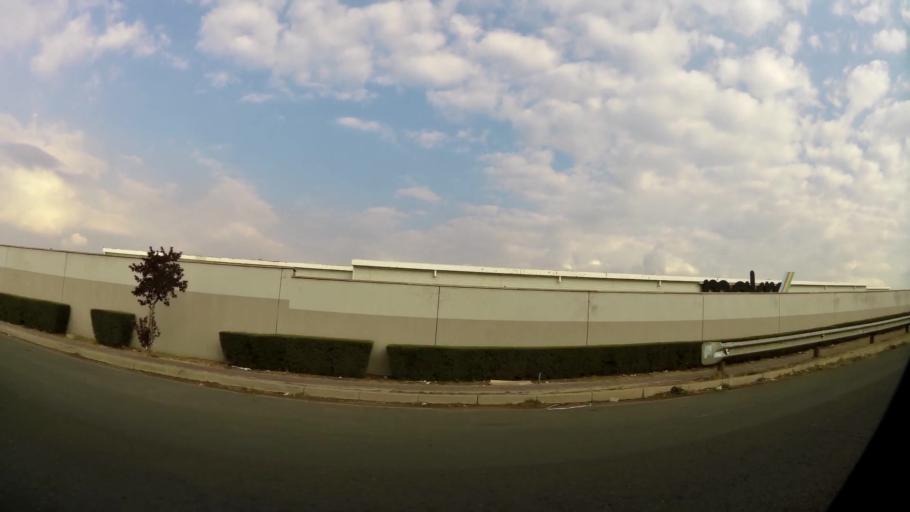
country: ZA
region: Gauteng
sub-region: Sedibeng District Municipality
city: Vanderbijlpark
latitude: -26.6987
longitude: 27.8810
